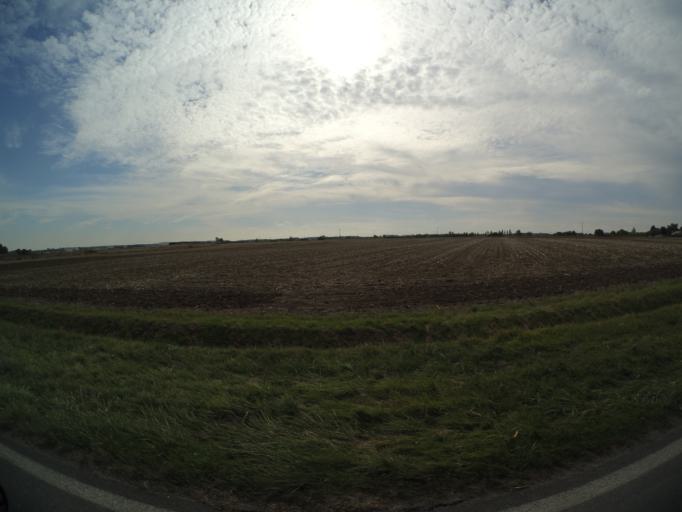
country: FR
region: Pays de la Loire
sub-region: Departement de Maine-et-Loire
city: Doue-la-Fontaine
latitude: 47.1962
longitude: -0.2534
